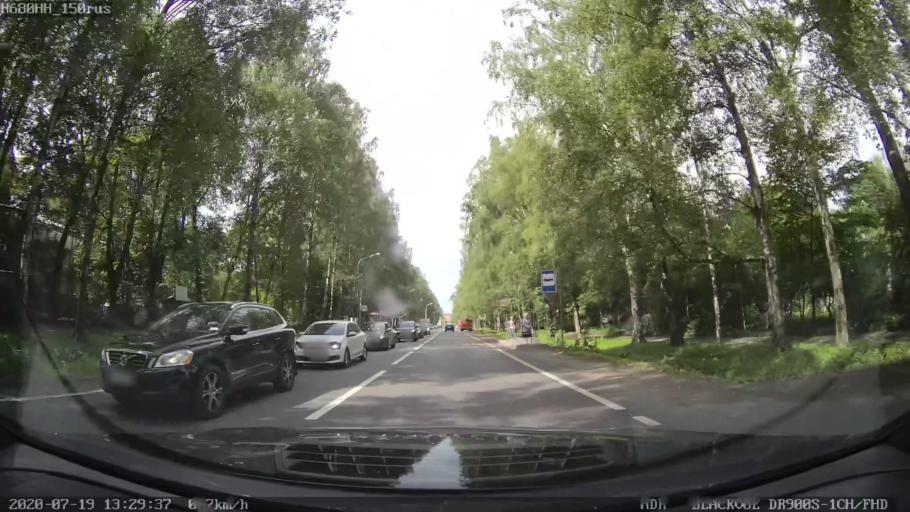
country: RU
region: St.-Petersburg
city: Pavlovsk
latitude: 59.7136
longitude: 30.4280
